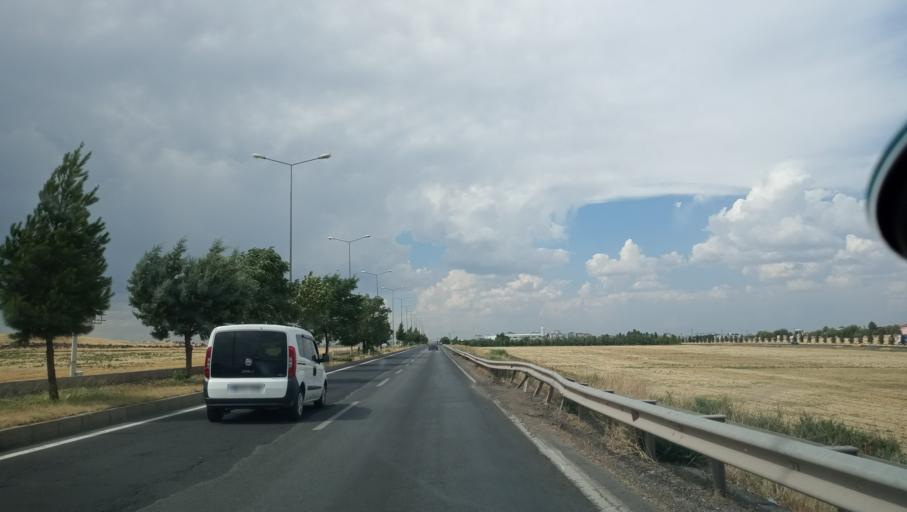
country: TR
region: Diyarbakir
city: Diyarbakir
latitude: 37.8768
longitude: 40.2207
